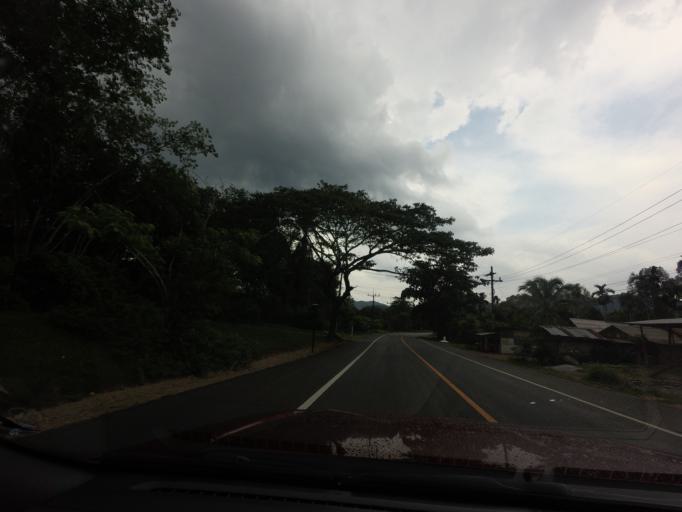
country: TH
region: Yala
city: Ban Nang Sata
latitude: 6.2283
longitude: 101.2208
